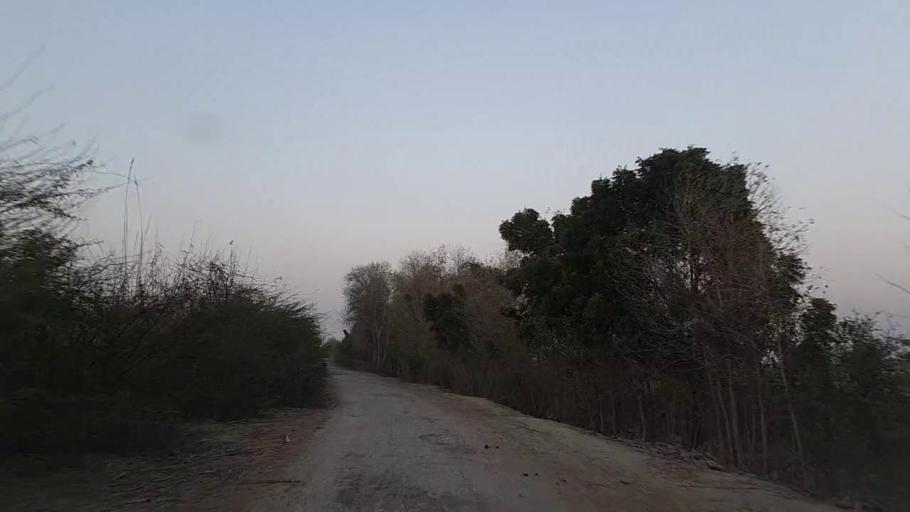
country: PK
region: Sindh
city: Bandhi
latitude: 26.6069
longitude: 68.3750
